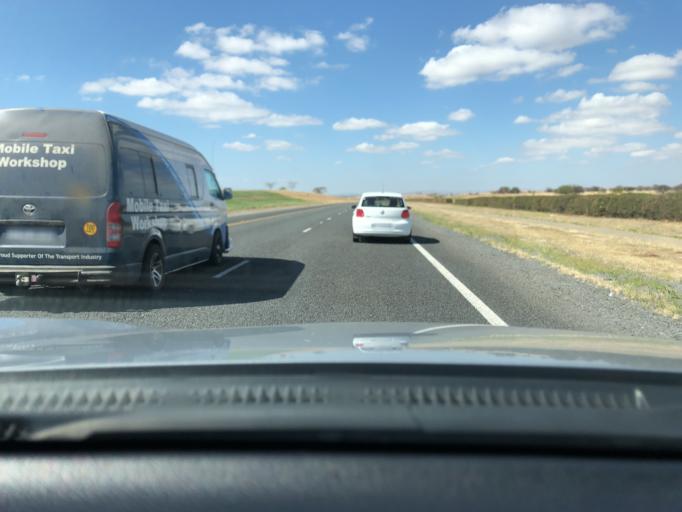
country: ZA
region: KwaZulu-Natal
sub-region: uThukela District Municipality
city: Estcourt
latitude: -28.8388
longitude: 29.7123
